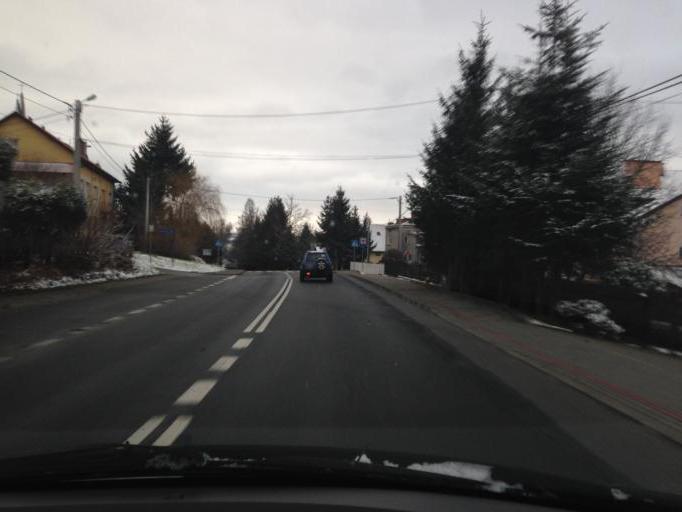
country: PL
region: Lesser Poland Voivodeship
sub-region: Powiat tarnowski
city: Gromnik
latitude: 49.8397
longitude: 20.9532
